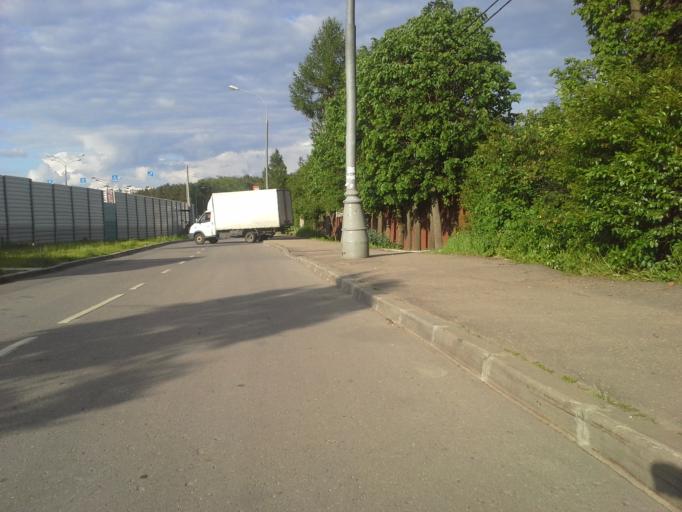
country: RU
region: Moscow
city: Novo-Peredelkino
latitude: 55.6336
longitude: 37.3441
